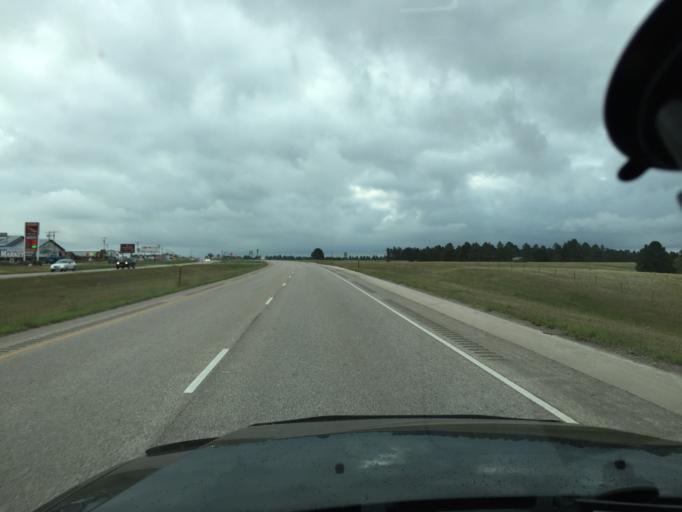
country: US
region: South Dakota
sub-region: Pennington County
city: Colonial Pine Hills
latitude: 43.9695
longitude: -103.3355
